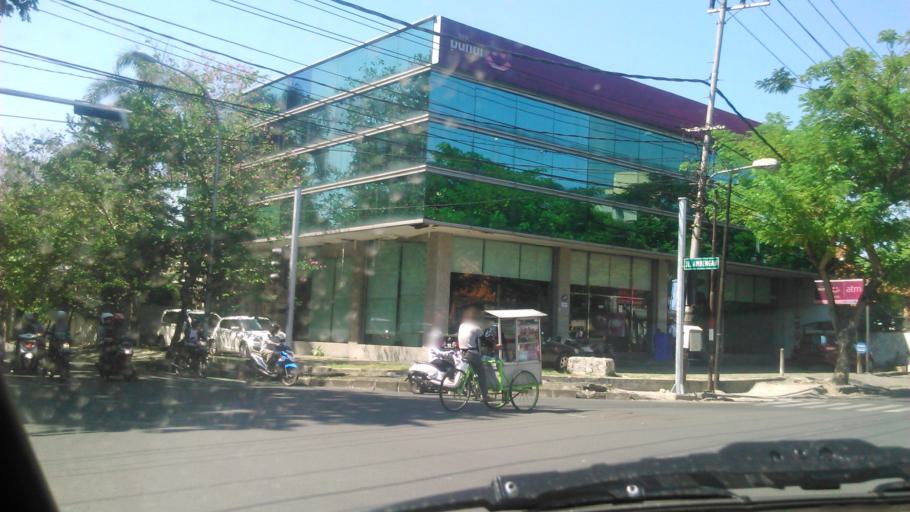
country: ID
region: East Java
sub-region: Kota Surabaya
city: Surabaya
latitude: -7.2560
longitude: 112.7468
